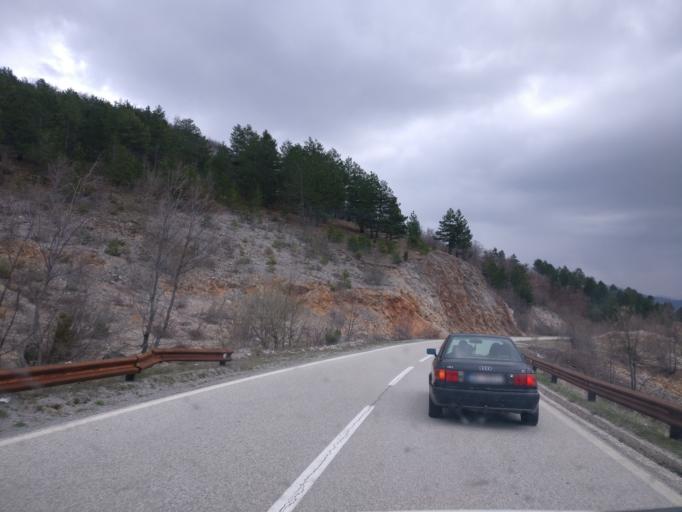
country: ME
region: Opstina Niksic
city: Niksic
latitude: 42.9377
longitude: 18.9320
